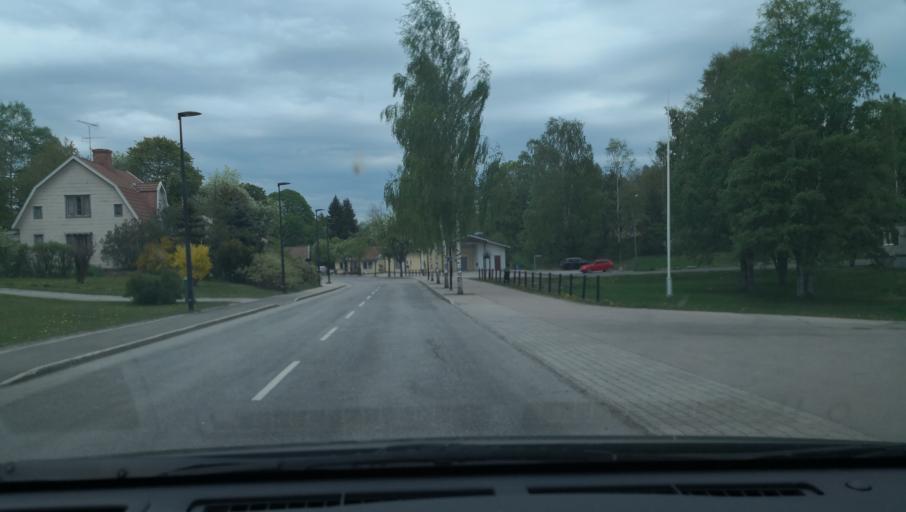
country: SE
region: Vaestmanland
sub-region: Skinnskattebergs Kommun
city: Skinnskatteberg
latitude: 59.8297
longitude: 15.6929
